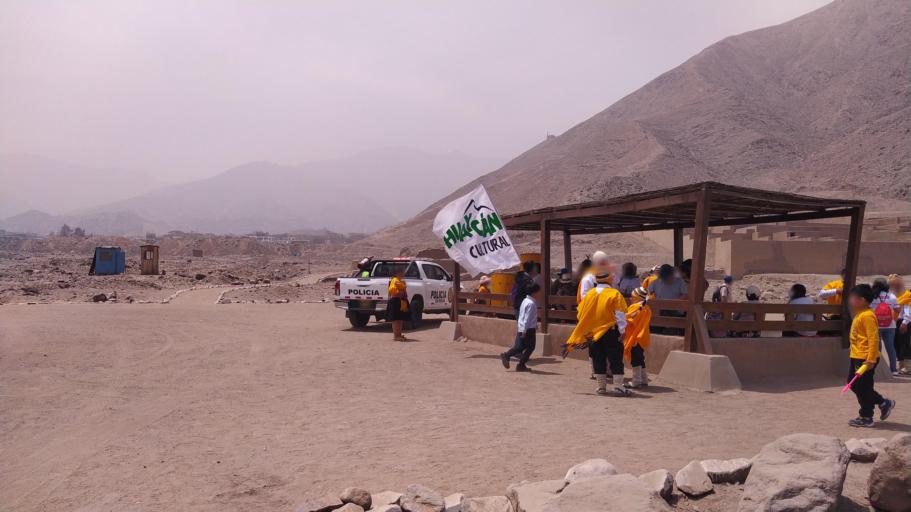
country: PE
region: Lima
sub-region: Lima
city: Santa Maria
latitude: -12.0123
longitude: -76.8316
